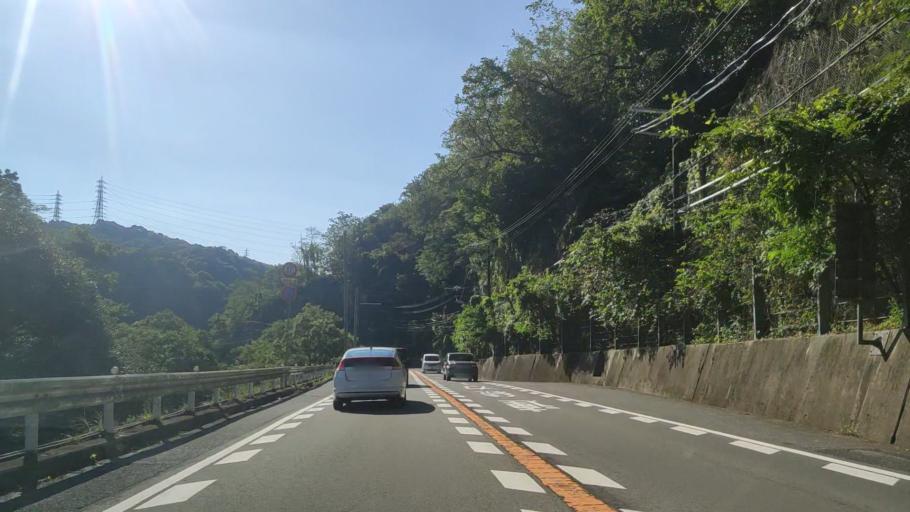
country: JP
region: Hyogo
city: Kobe
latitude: 34.7102
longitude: 135.1594
